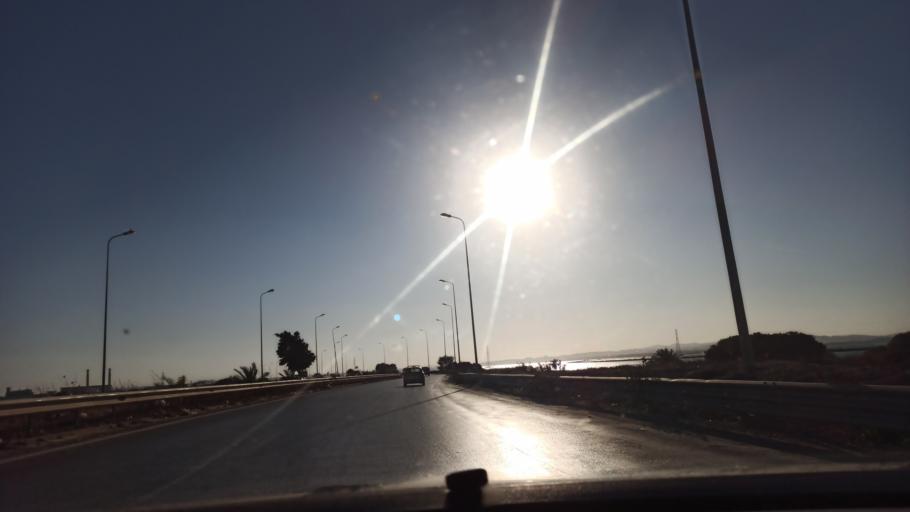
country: TN
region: Tunis
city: La Goulette
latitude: 36.8248
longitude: 10.3059
